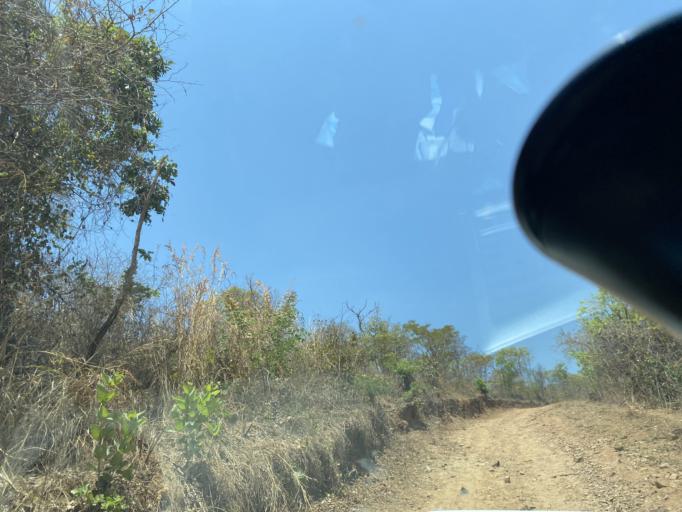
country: ZM
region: Lusaka
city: Kafue
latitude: -15.8074
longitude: 28.4363
